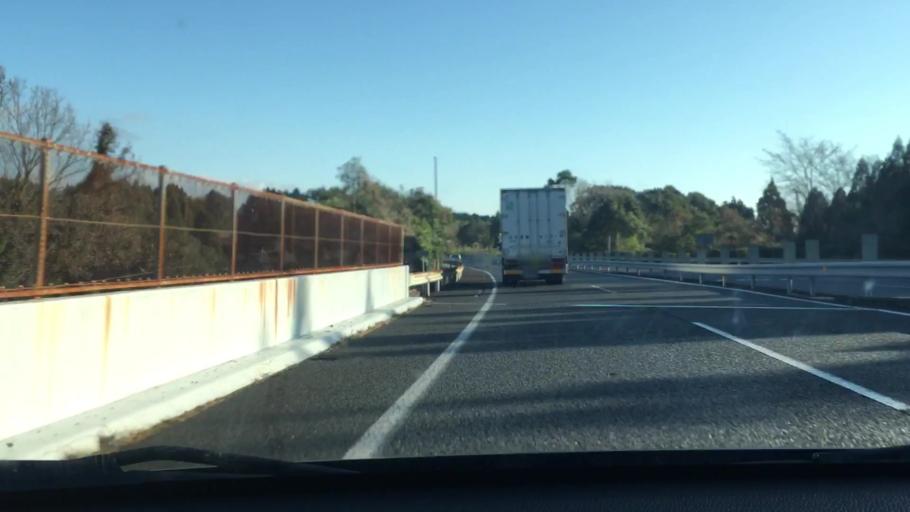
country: JP
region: Kagoshima
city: Kajiki
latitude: 31.8230
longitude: 130.6943
